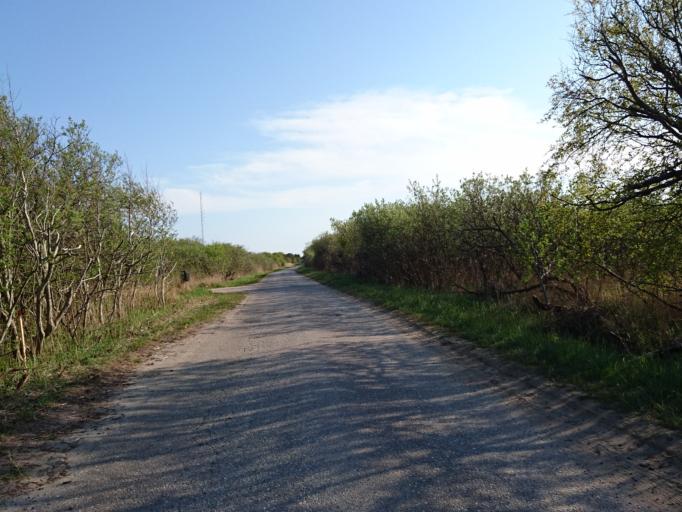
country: DK
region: North Denmark
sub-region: Frederikshavn Kommune
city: Skagen
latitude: 57.7474
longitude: 10.6028
